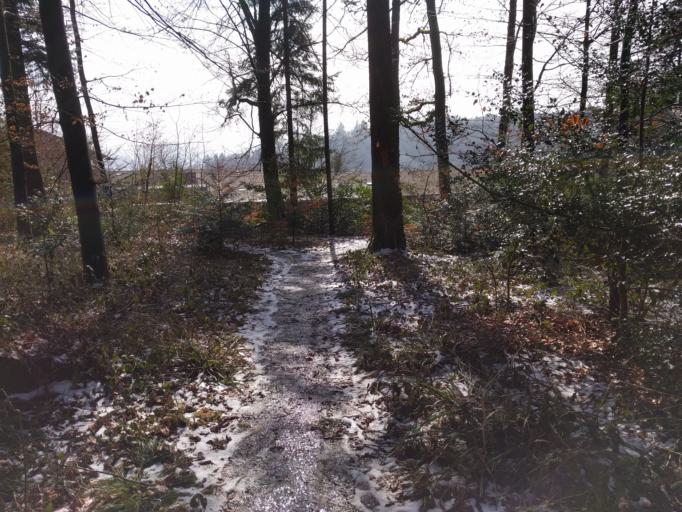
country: CH
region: Aargau
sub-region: Bezirk Aarau
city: Aarau
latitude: 47.4043
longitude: 8.0400
